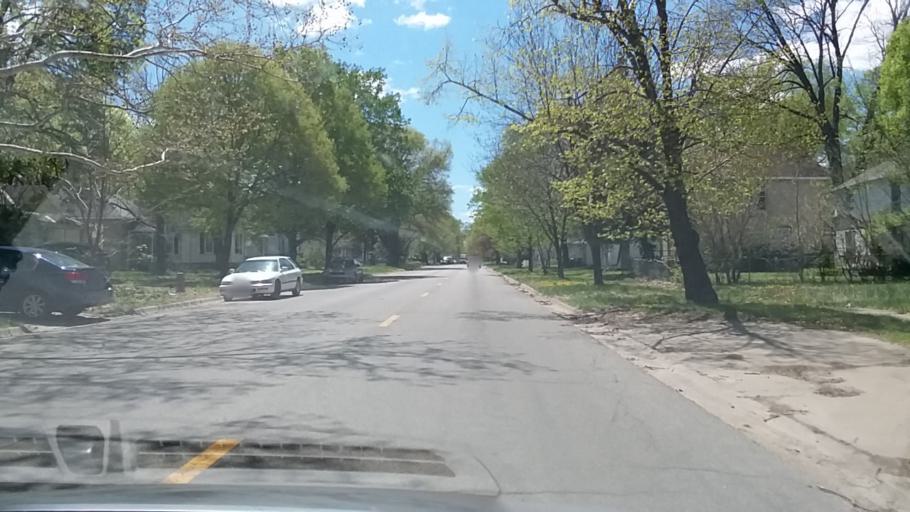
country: US
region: Kansas
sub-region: Douglas County
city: Lawrence
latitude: 38.9652
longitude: -95.2324
